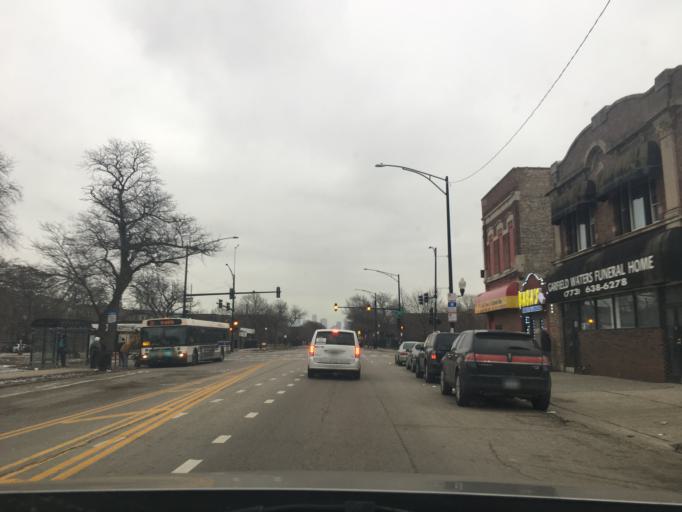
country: US
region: Illinois
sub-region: Cook County
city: Cicero
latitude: 41.8809
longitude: -87.7119
